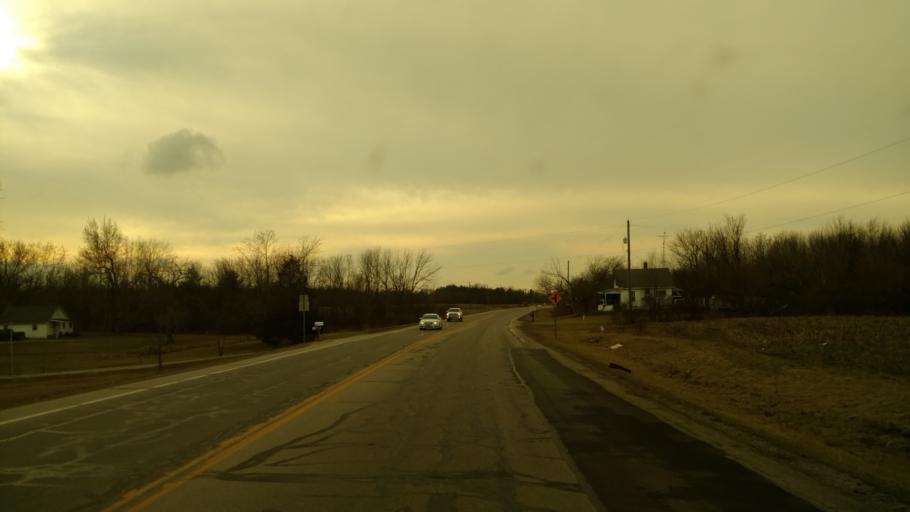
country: US
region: Ohio
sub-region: Crawford County
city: Crestline
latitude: 40.7799
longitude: -82.6637
